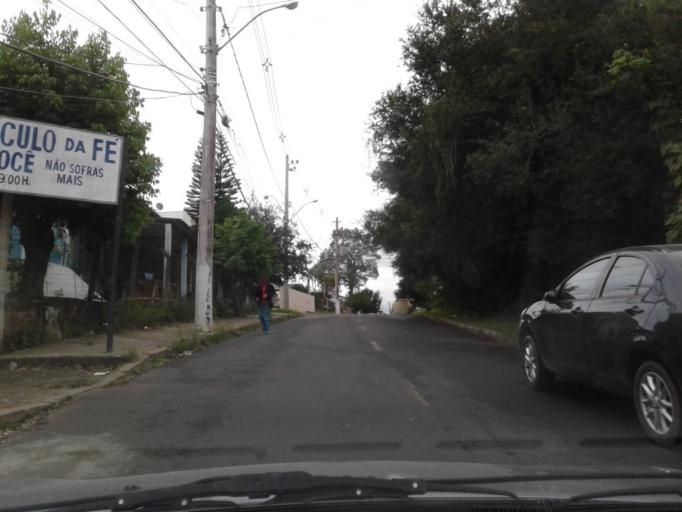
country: BR
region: Rio Grande do Sul
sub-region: Gravatai
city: Gravatai
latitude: -29.9373
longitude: -51.0050
